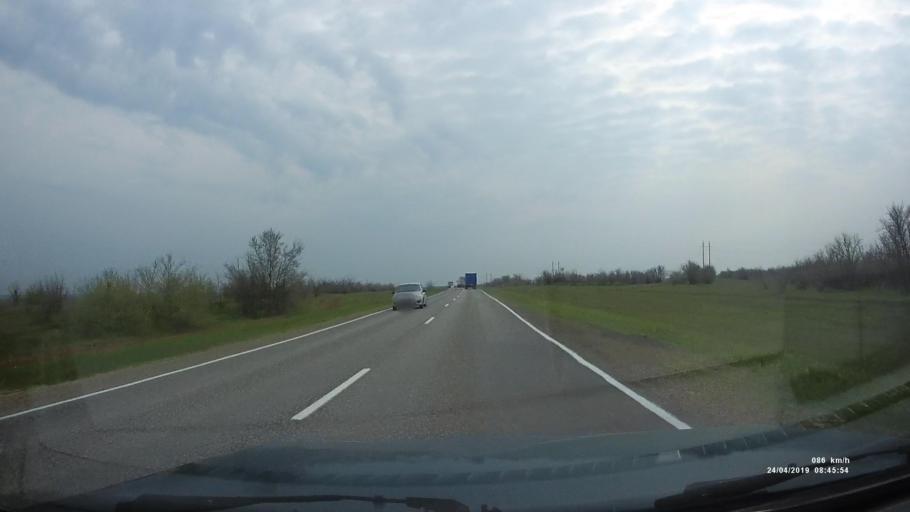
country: RU
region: Kalmykiya
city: Arshan'
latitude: 46.2365
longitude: 44.0699
